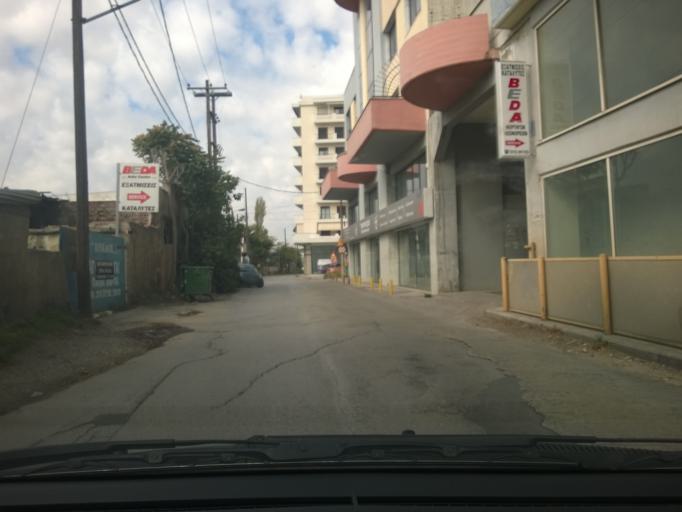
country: GR
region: Central Macedonia
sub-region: Nomos Thessalonikis
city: Menemeni
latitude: 40.6527
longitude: 22.9086
